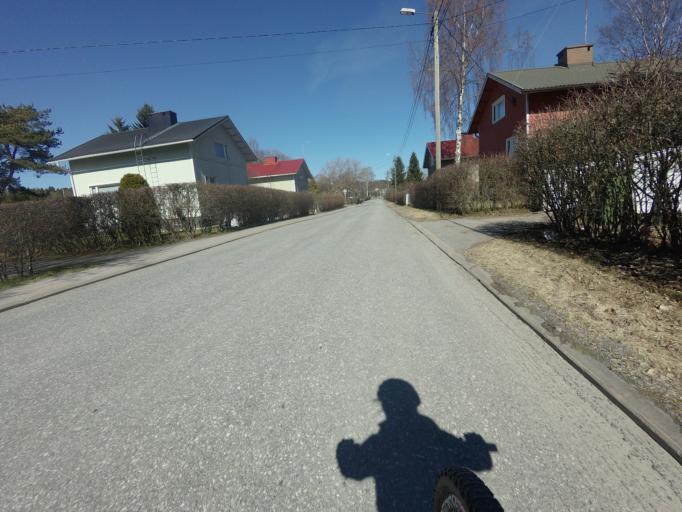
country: FI
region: Varsinais-Suomi
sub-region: Turku
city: Raisio
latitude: 60.4500
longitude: 22.1572
